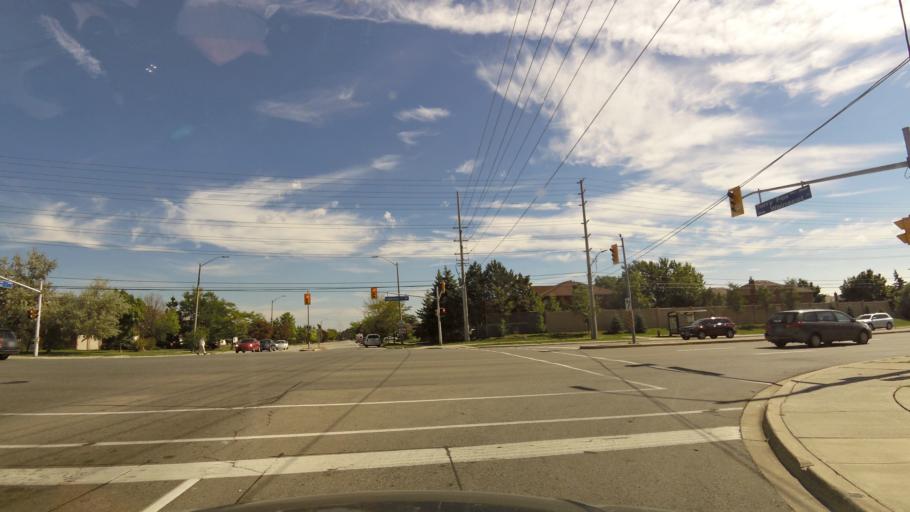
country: CA
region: Ontario
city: Mississauga
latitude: 43.5877
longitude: -79.6747
